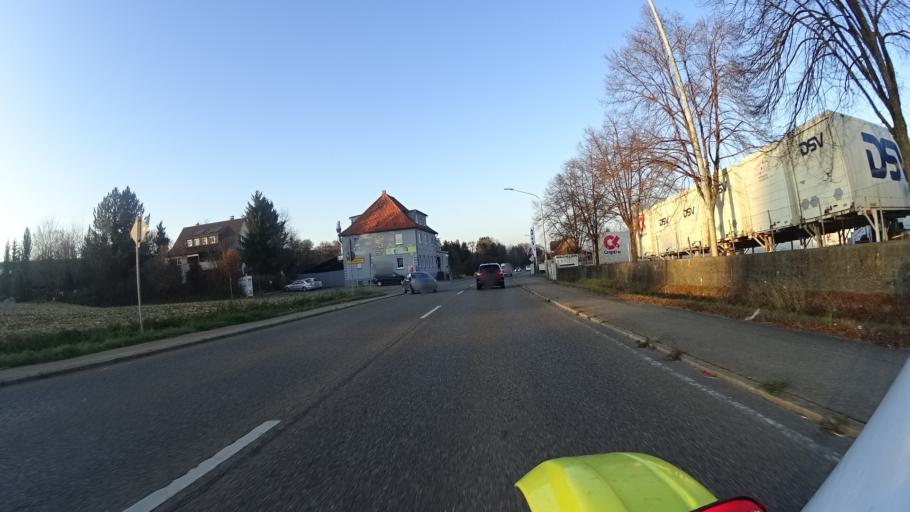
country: DE
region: Baden-Wuerttemberg
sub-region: Regierungsbezirk Stuttgart
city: Eislingen
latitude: 48.6754
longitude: 9.6879
